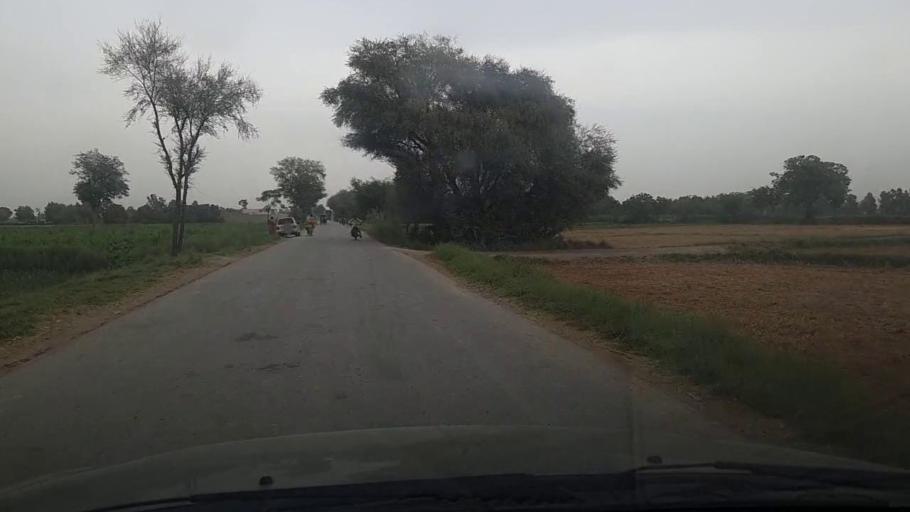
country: PK
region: Sindh
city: Daulatpur
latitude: 26.3183
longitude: 68.1034
